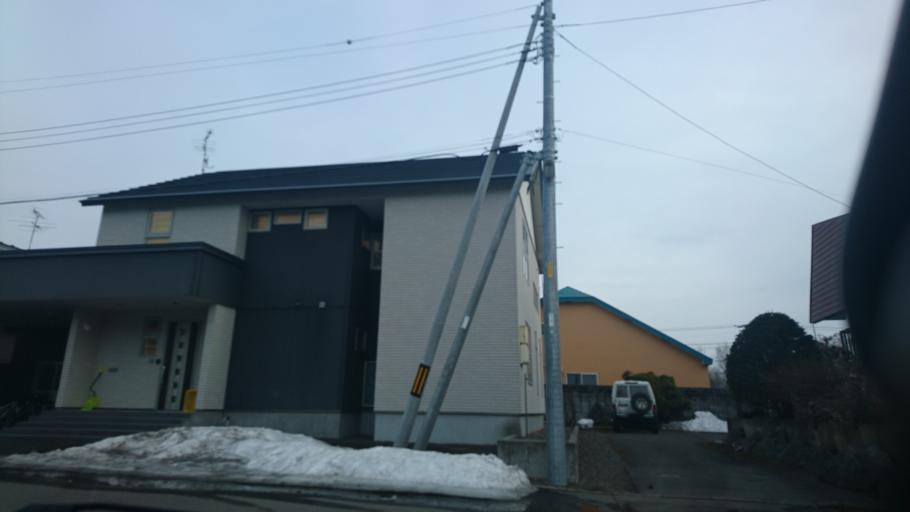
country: JP
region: Hokkaido
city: Otofuke
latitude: 42.9919
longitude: 143.1897
